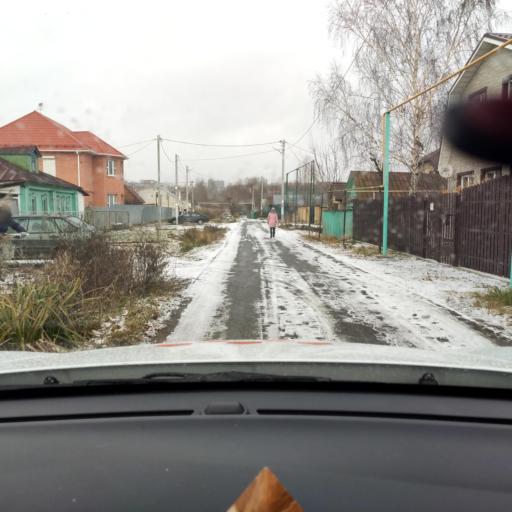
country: RU
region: Tatarstan
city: Verkhniy Uslon
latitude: 55.8005
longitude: 49.0372
